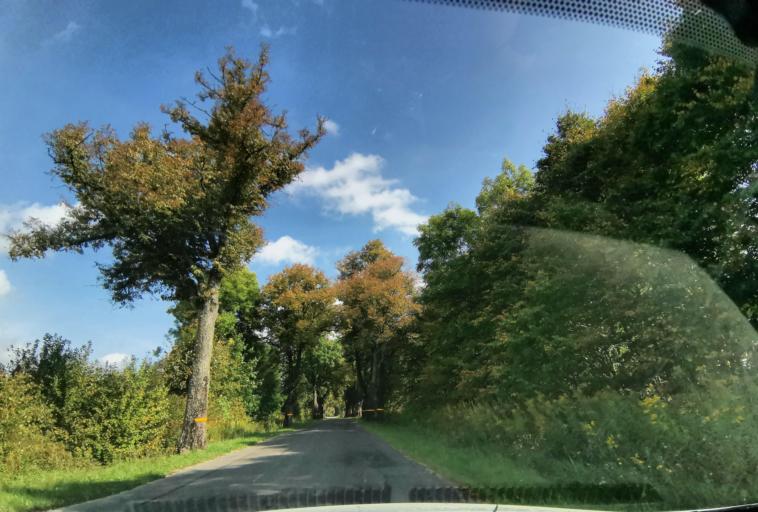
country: RU
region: Kaliningrad
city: Chernyakhovsk
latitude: 54.6596
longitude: 21.9180
